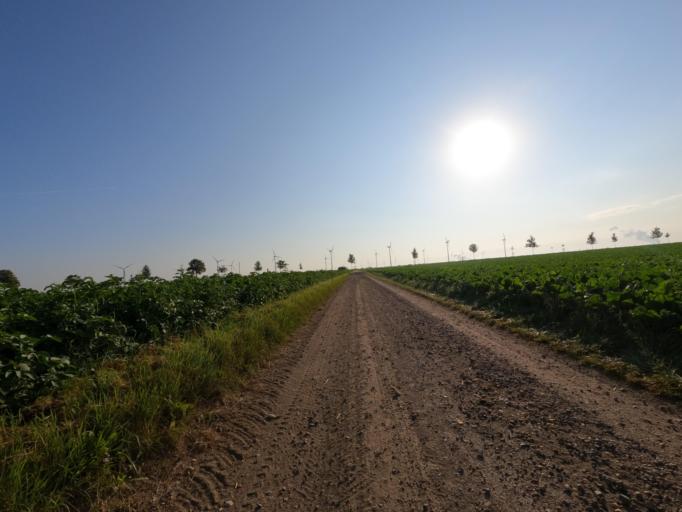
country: DE
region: North Rhine-Westphalia
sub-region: Regierungsbezirk Koln
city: Titz
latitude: 51.0189
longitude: 6.4725
